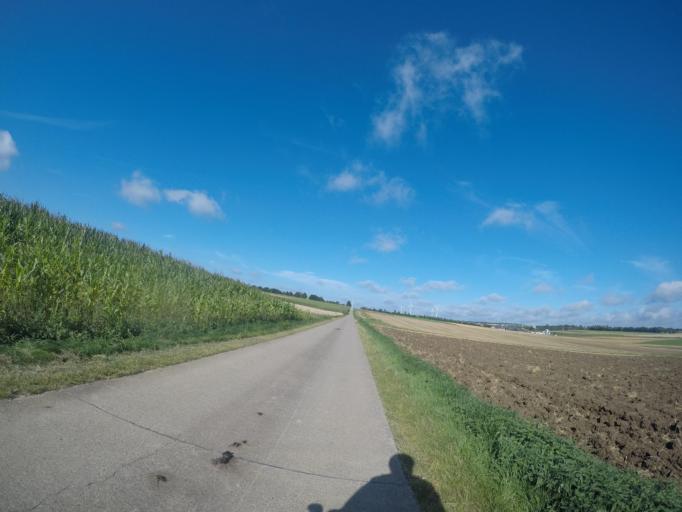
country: DE
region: Baden-Wuerttemberg
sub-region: Tuebingen Region
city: Schelklingen
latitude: 48.3870
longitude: 9.6545
